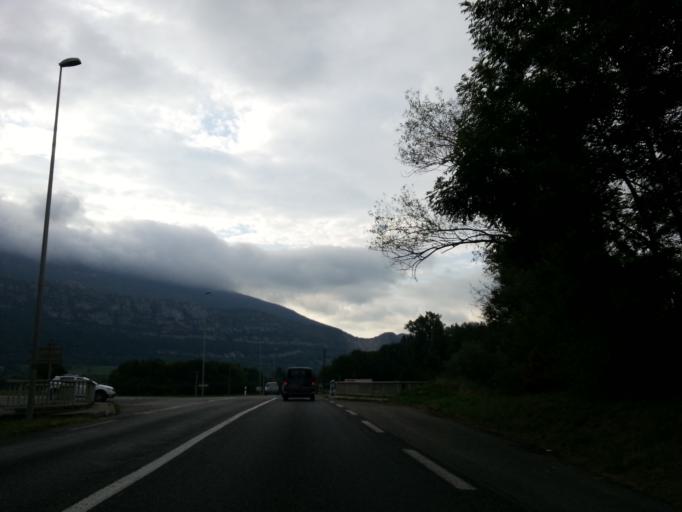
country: FR
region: Rhone-Alpes
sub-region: Departement de la Haute-Savoie
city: Doussard
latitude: 45.7839
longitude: 6.2251
